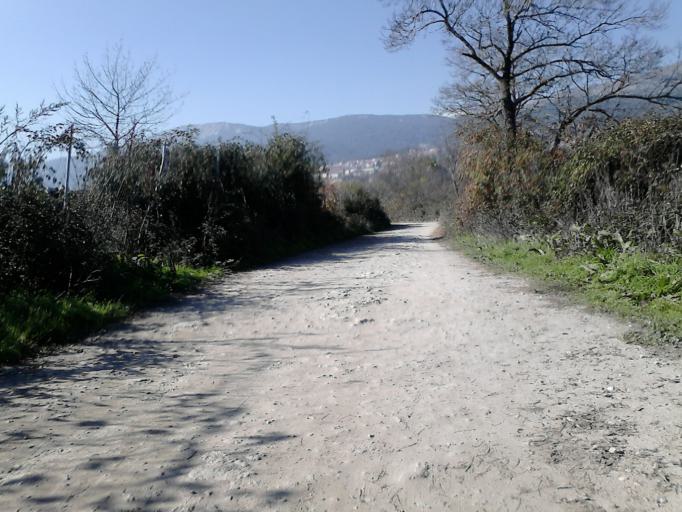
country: ES
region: Madrid
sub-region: Provincia de Madrid
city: El Escorial
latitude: 40.5894
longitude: -4.1218
